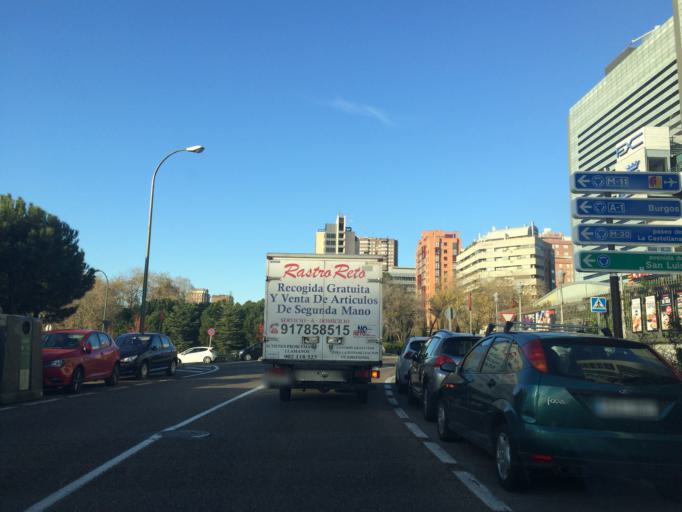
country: ES
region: Madrid
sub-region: Provincia de Madrid
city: Pinar de Chamartin
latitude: 40.4728
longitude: -3.6723
